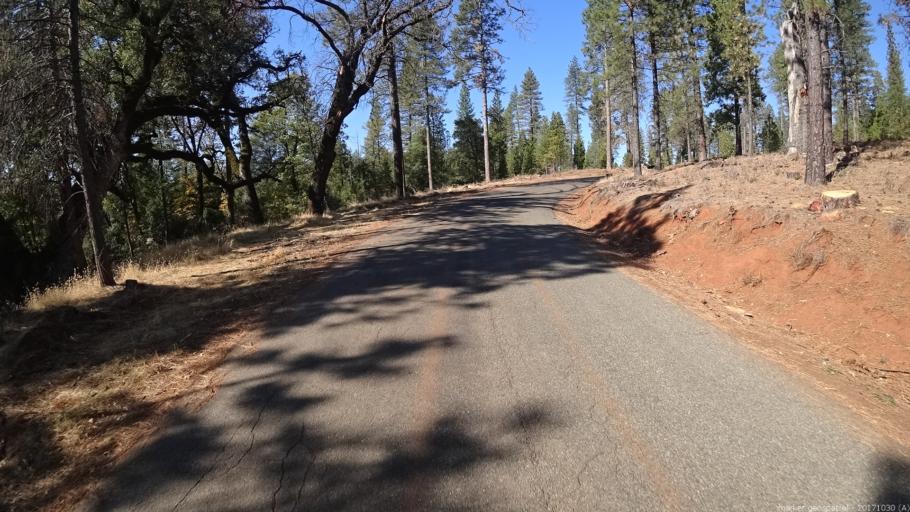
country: US
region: California
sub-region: Shasta County
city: Shingletown
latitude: 40.6067
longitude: -121.8575
